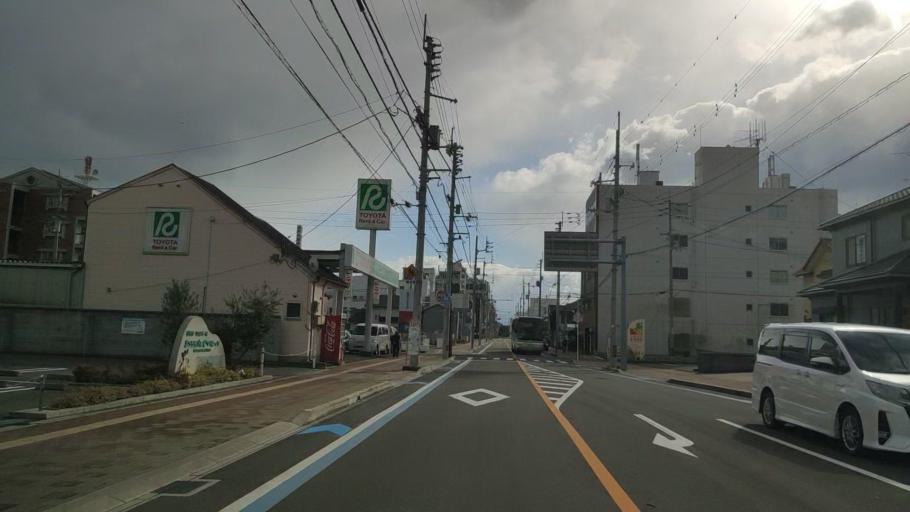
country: JP
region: Ehime
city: Hojo
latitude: 34.0669
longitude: 132.9919
